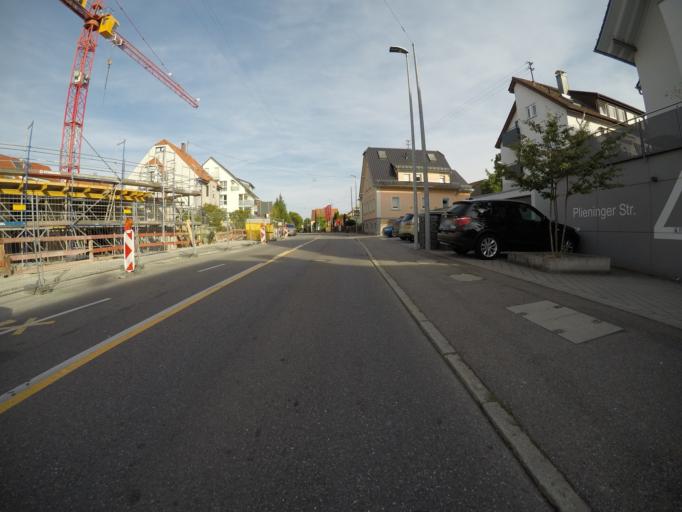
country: DE
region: Baden-Wuerttemberg
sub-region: Regierungsbezirk Stuttgart
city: Leinfelden-Echterdingen
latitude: 48.6908
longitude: 9.1680
